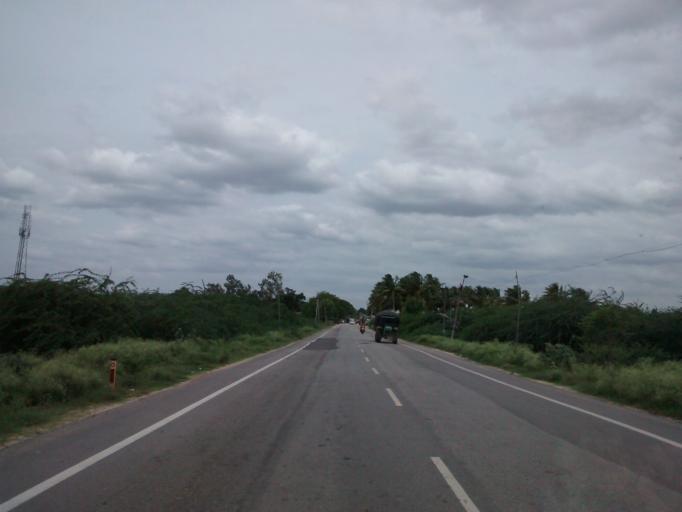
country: IN
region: Andhra Pradesh
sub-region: Chittoor
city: Chittoor
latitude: 13.2806
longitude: 79.0412
